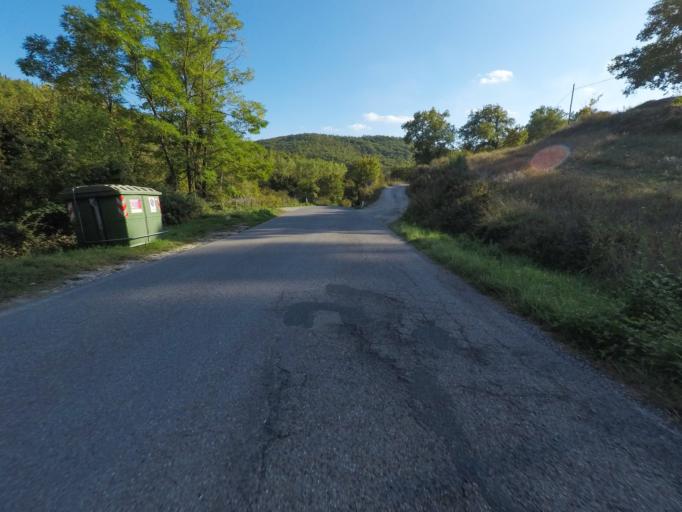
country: IT
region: Tuscany
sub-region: Provincia di Siena
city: Radda in Chianti
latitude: 43.4715
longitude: 11.3741
